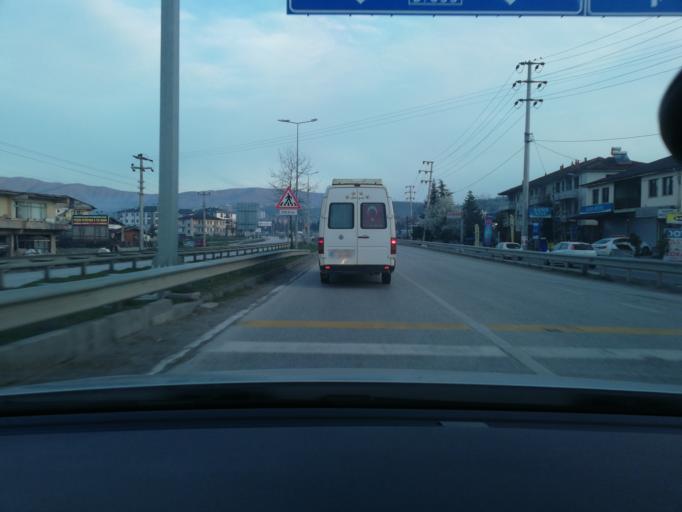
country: TR
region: Duzce
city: Konuralp
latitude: 40.8935
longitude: 31.1674
